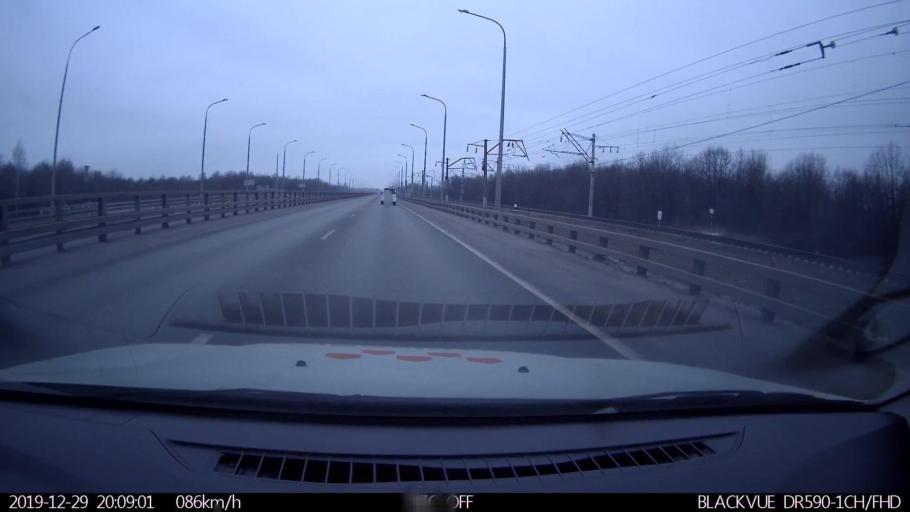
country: RU
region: Nizjnij Novgorod
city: Neklyudovo
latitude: 56.3794
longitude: 43.9571
